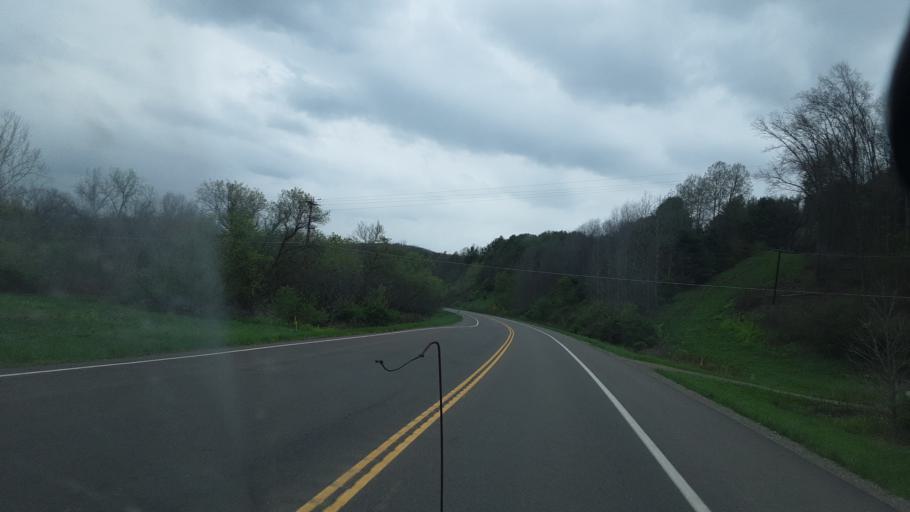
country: US
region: New York
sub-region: Steuben County
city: Addison
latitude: 42.0802
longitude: -77.2706
